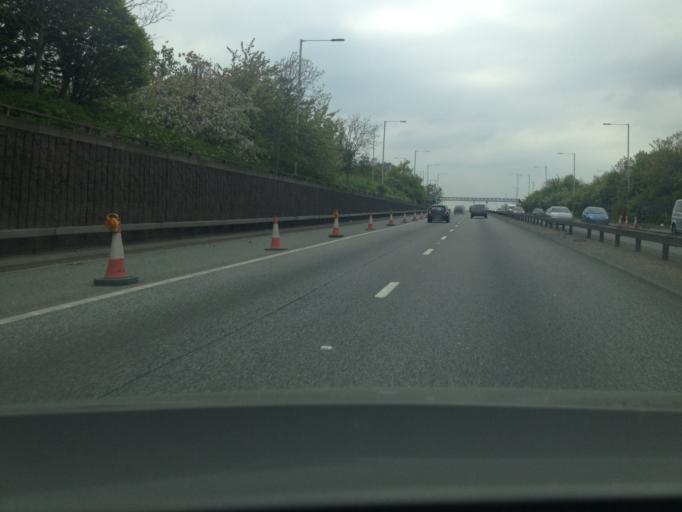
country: GB
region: England
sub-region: Greater London
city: Northolt
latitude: 51.5434
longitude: -0.3794
